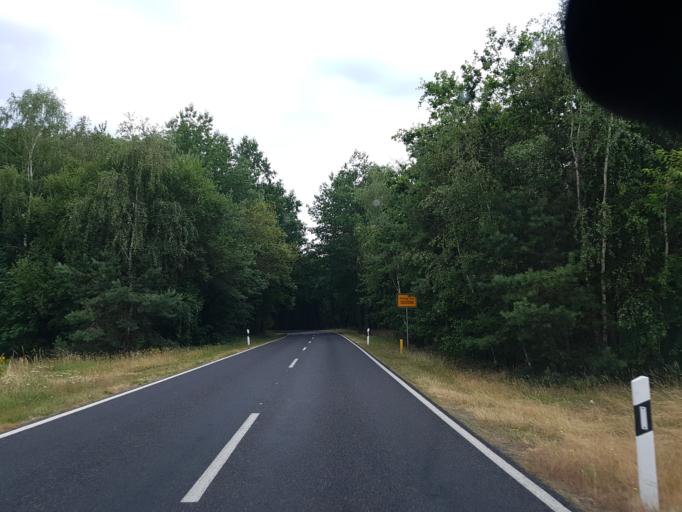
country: DE
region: Brandenburg
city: Sallgast
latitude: 51.5821
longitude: 13.8494
